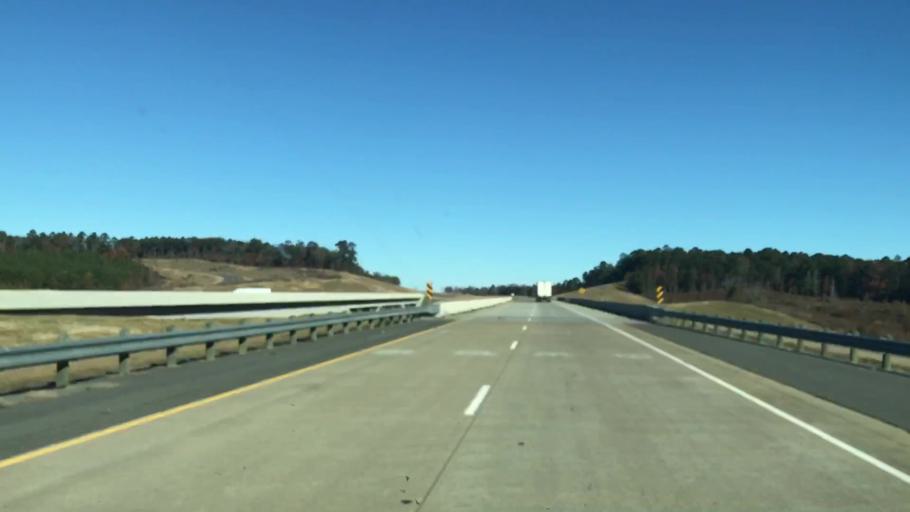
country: US
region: Louisiana
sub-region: Caddo Parish
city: Vivian
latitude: 32.9421
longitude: -93.8974
